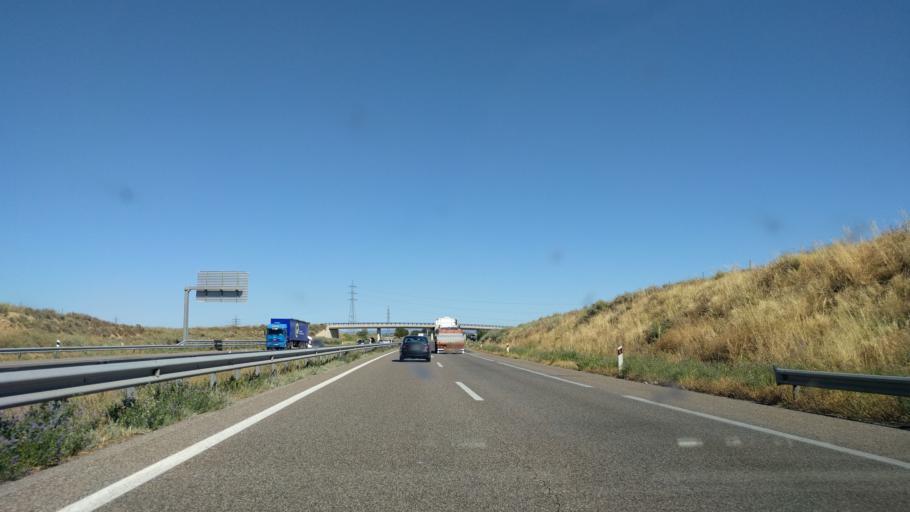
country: ES
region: Catalonia
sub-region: Provincia de Lleida
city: Alcoletge
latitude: 41.6358
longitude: 0.6872
